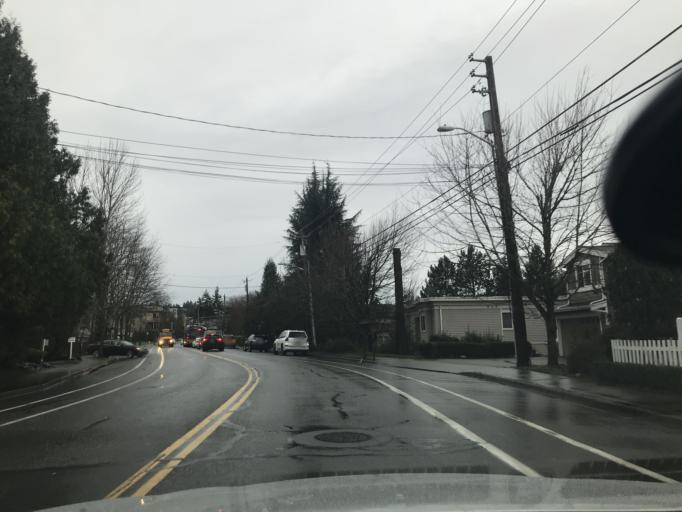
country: US
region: Washington
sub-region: King County
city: Kirkland
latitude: 47.6690
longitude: -122.2024
